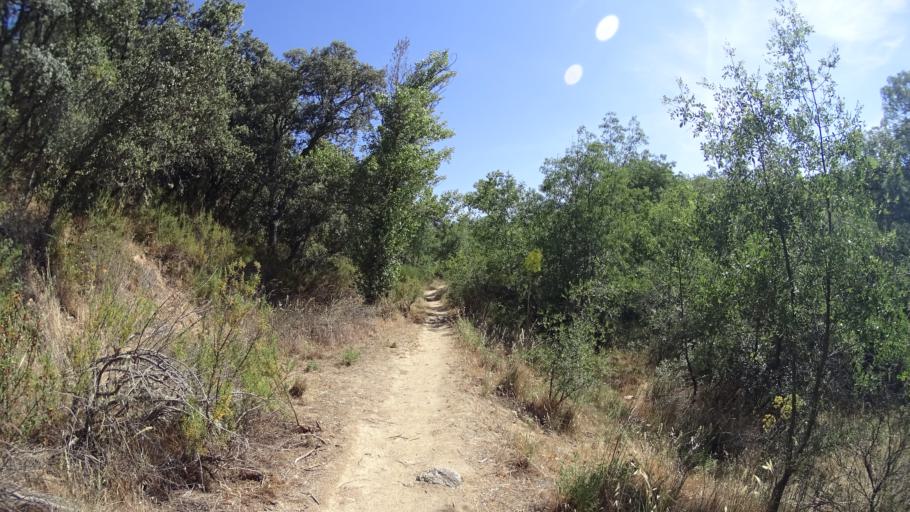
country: ES
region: Madrid
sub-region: Provincia de Madrid
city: Torrelodones
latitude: 40.5908
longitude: -3.9619
